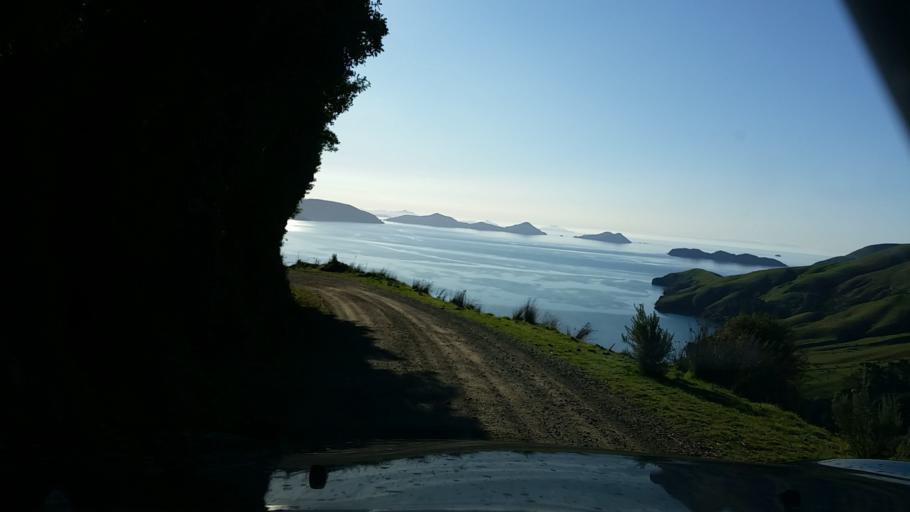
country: NZ
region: Marlborough
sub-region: Marlborough District
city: Picton
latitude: -41.0257
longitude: 174.1491
